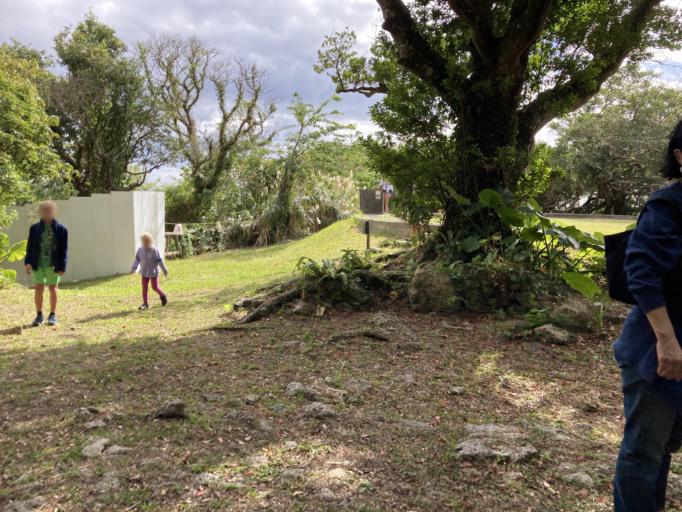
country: JP
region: Okinawa
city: Tomigusuku
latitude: 26.1433
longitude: 127.7832
